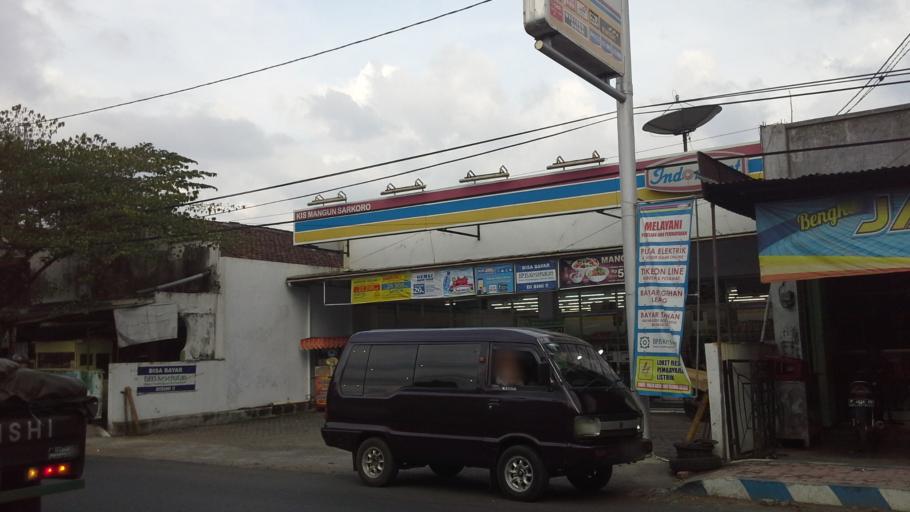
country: ID
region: East Java
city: Bondowoso
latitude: -7.9225
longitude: 113.8269
